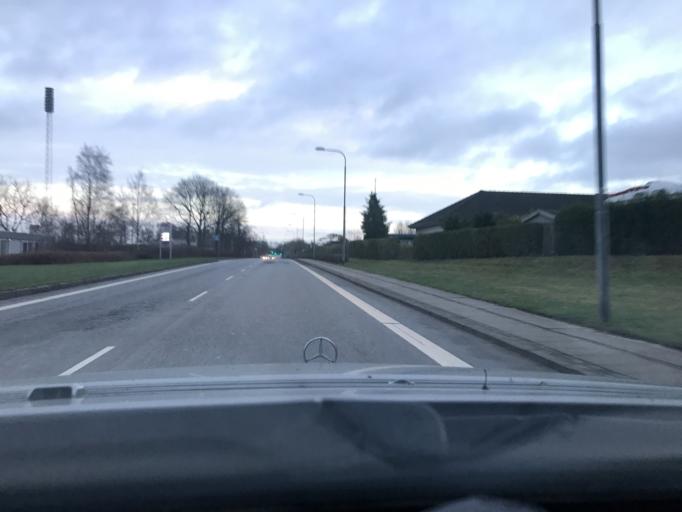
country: DK
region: South Denmark
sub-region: Sonderborg Kommune
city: Nordborg
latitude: 55.0556
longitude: 9.7396
